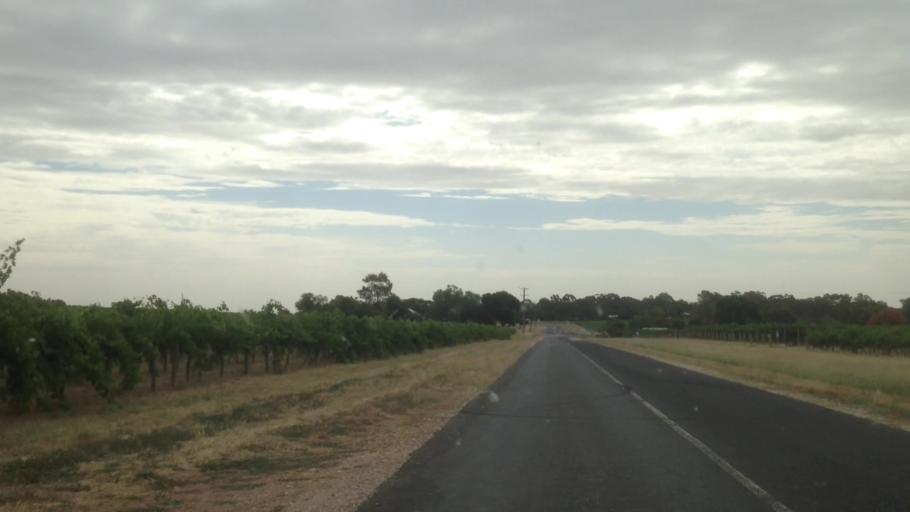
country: AU
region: South Australia
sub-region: Barossa
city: Lyndoch
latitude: -34.5978
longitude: 138.9230
